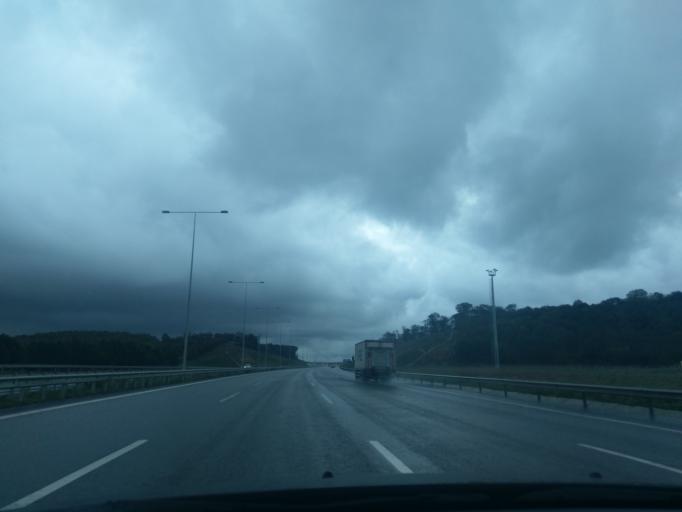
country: TR
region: Istanbul
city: Kemerburgaz
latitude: 41.2354
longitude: 28.8872
